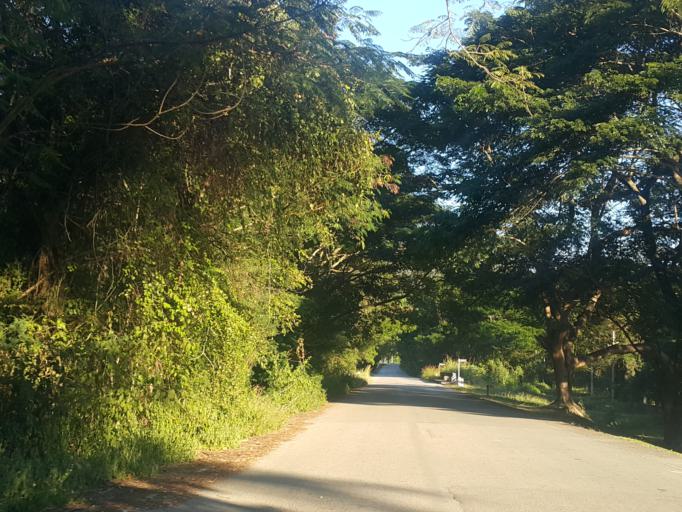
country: TH
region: Chiang Mai
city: San Sai
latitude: 18.9251
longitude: 99.1395
